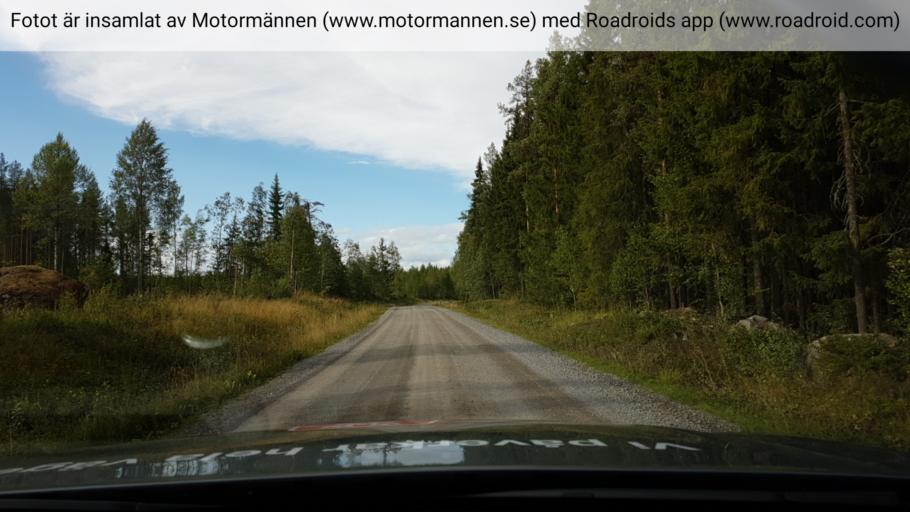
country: SE
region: Jaemtland
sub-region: Braecke Kommun
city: Braecke
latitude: 63.2690
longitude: 15.3781
